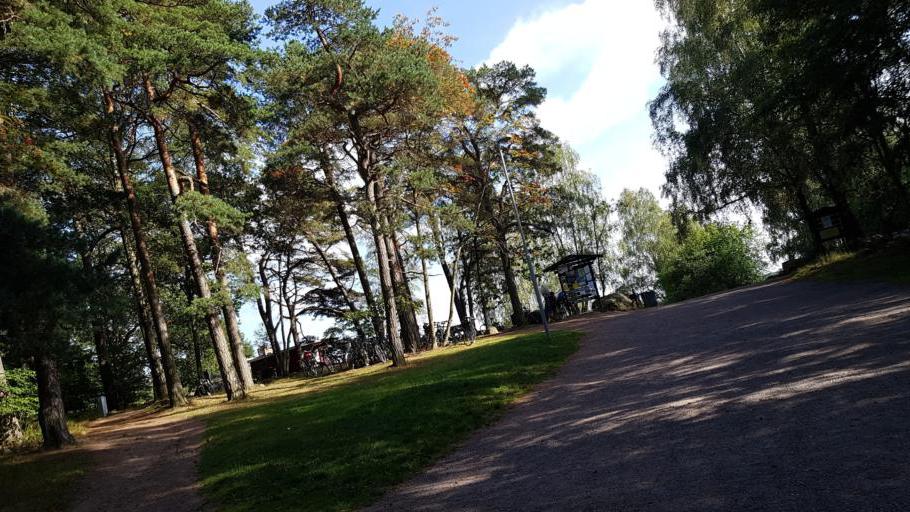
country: SE
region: Vaestra Goetaland
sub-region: Molndal
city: Moelndal
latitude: 57.6903
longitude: 12.0334
